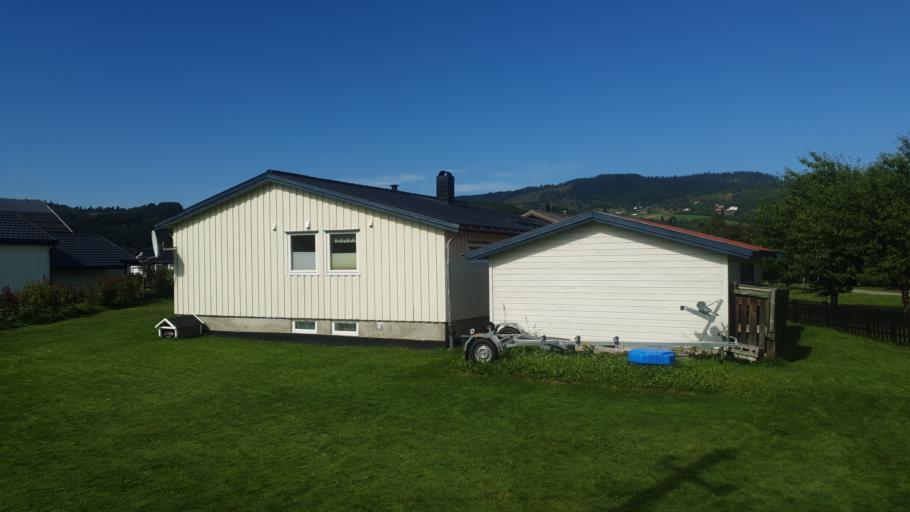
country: NO
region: Sor-Trondelag
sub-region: Orkdal
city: Orkanger
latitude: 63.2739
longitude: 9.8220
